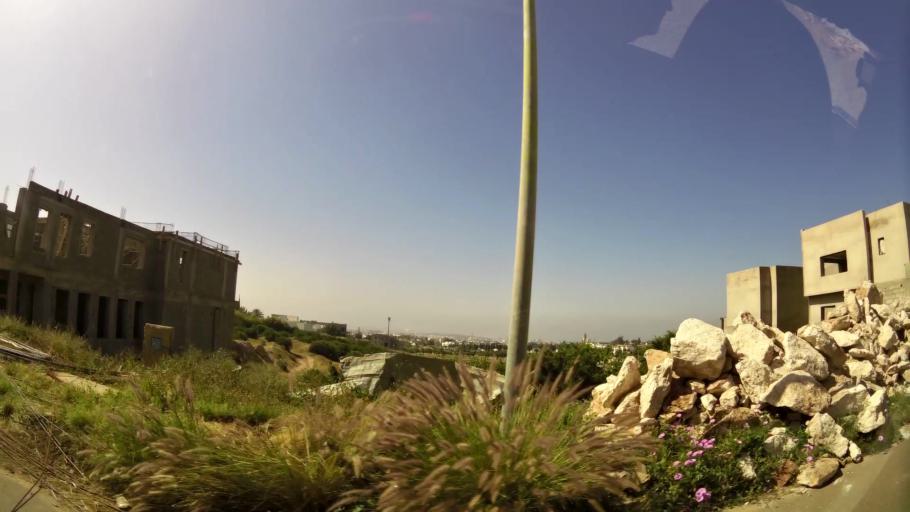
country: MA
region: Souss-Massa-Draa
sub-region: Agadir-Ida-ou-Tnan
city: Agadir
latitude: 30.4422
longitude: -9.5846
